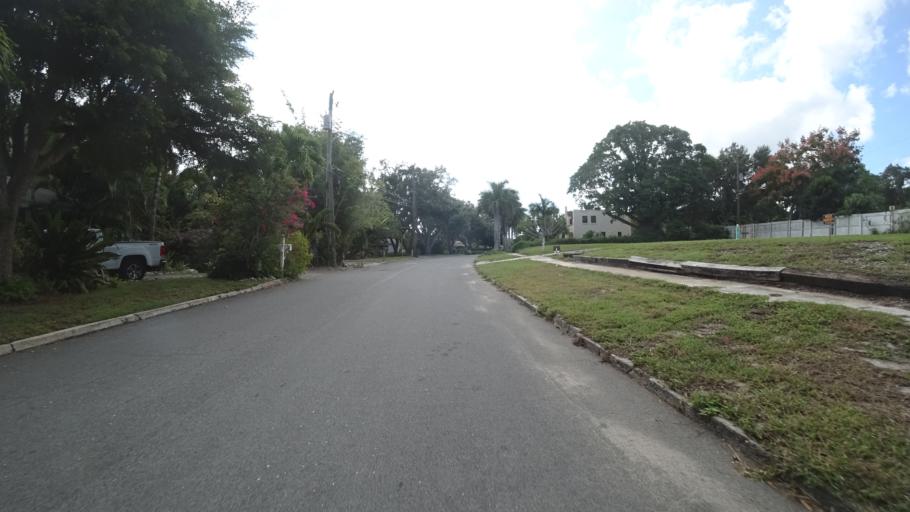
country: US
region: Florida
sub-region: Manatee County
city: West Bradenton
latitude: 27.5048
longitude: -82.6138
